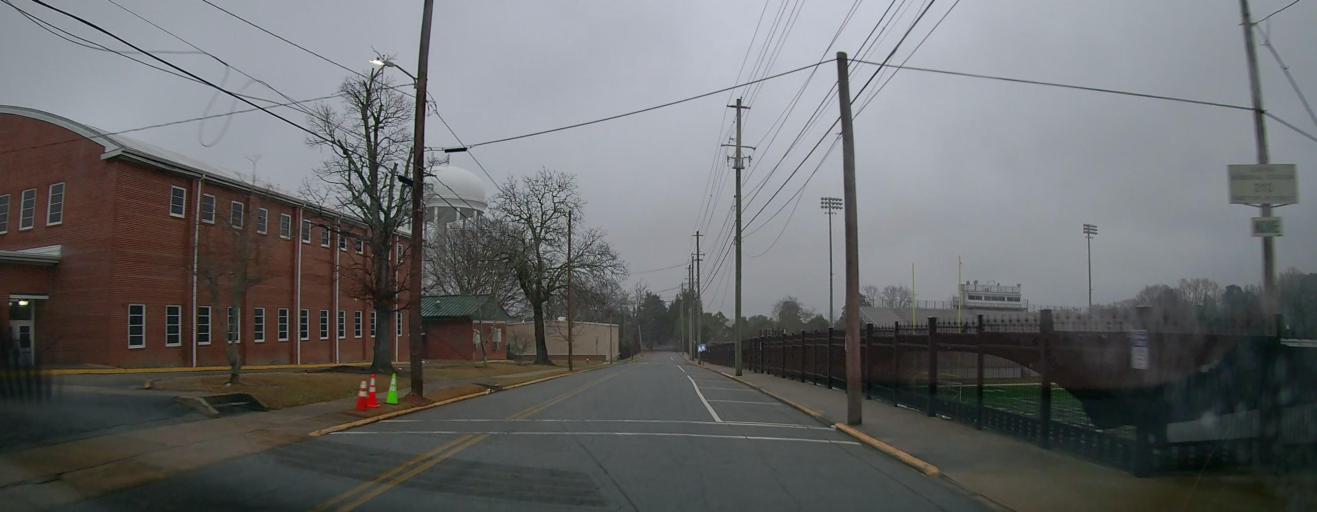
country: US
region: Georgia
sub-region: Spalding County
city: Griffin
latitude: 33.2457
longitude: -84.2600
